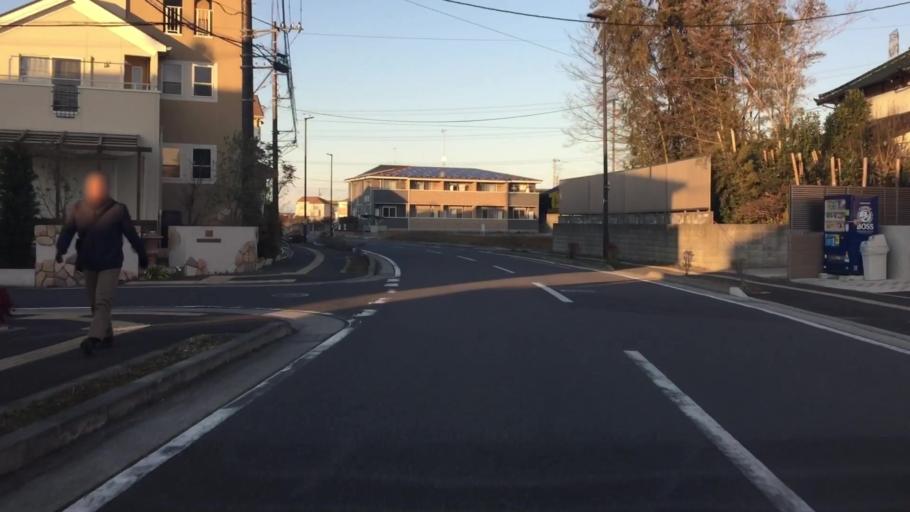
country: JP
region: Ibaraki
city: Moriya
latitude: 35.9158
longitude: 139.9553
